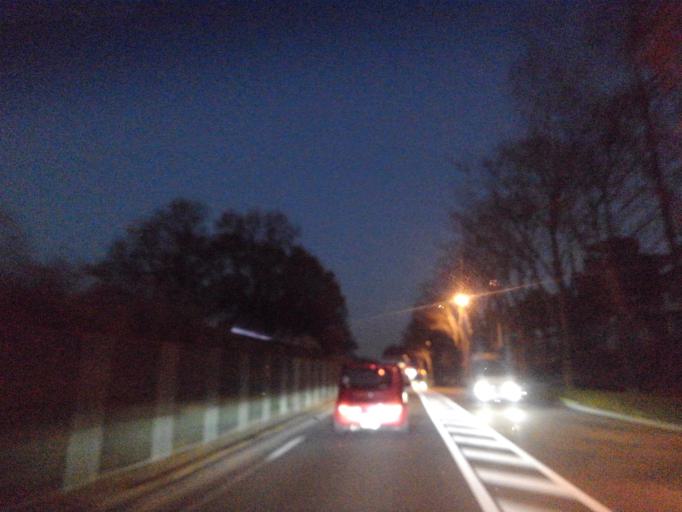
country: JP
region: Tokyo
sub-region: Machida-shi
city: Machida
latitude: 35.6156
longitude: 139.4509
